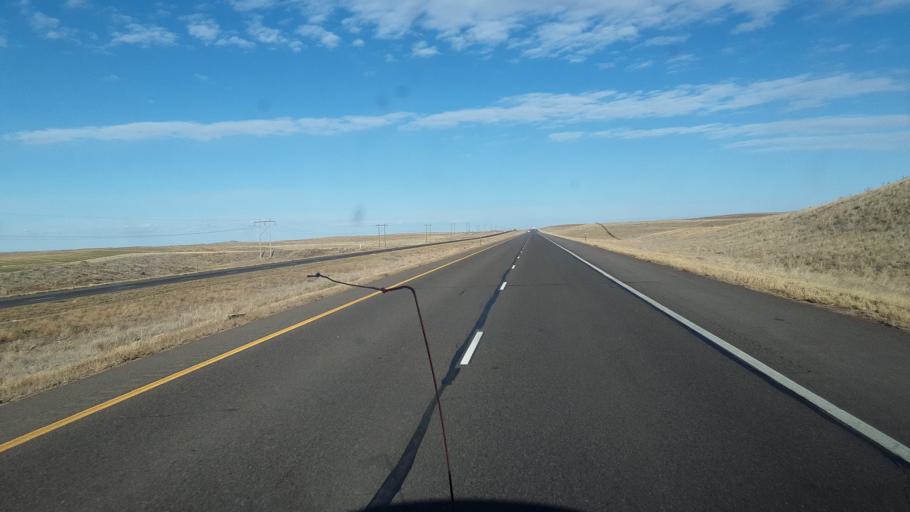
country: US
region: Colorado
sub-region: Morgan County
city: Brush
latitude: 40.3369
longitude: -103.4660
